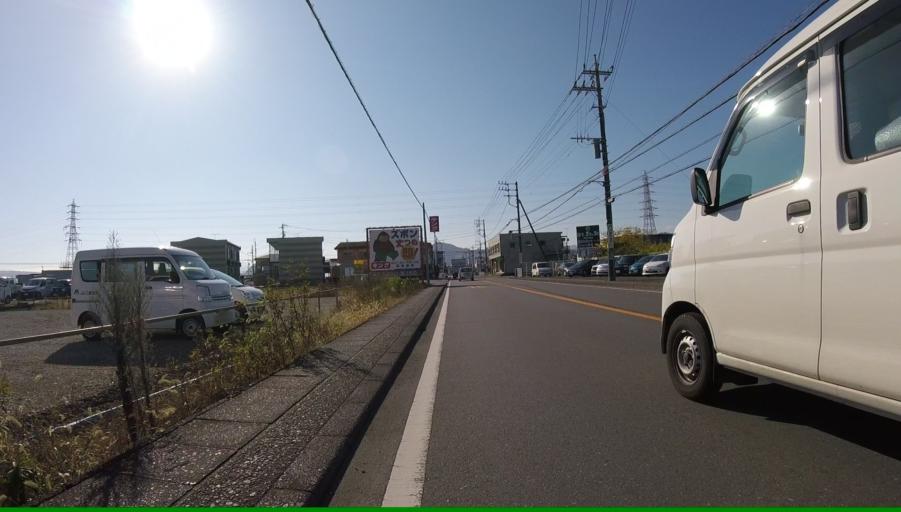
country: JP
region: Shizuoka
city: Mishima
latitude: 35.1027
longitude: 138.9157
